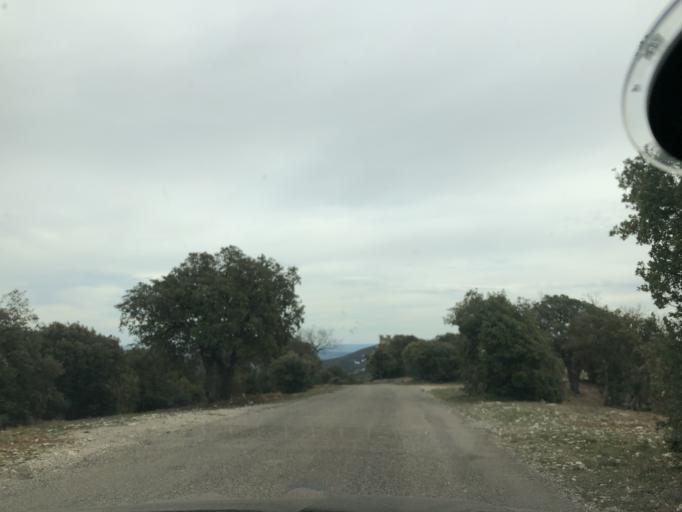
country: FR
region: Provence-Alpes-Cote d'Azur
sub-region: Departement du Vaucluse
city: Bonnieux
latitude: 43.8064
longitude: 5.3002
